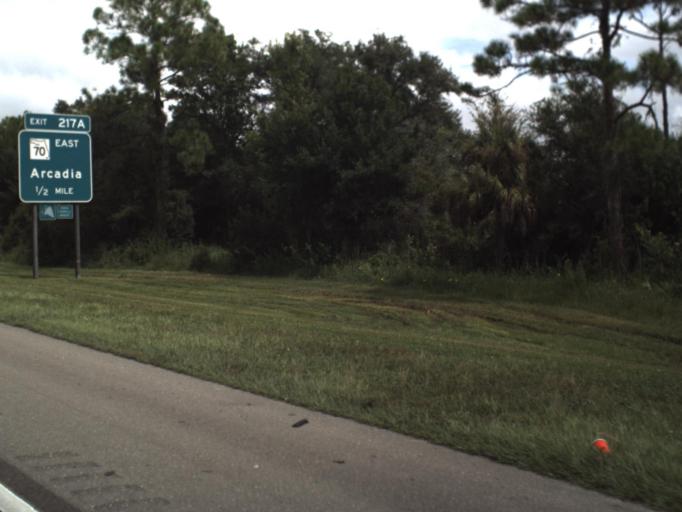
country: US
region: Florida
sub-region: Sarasota County
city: Desoto Lakes
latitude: 27.4286
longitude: -82.4592
